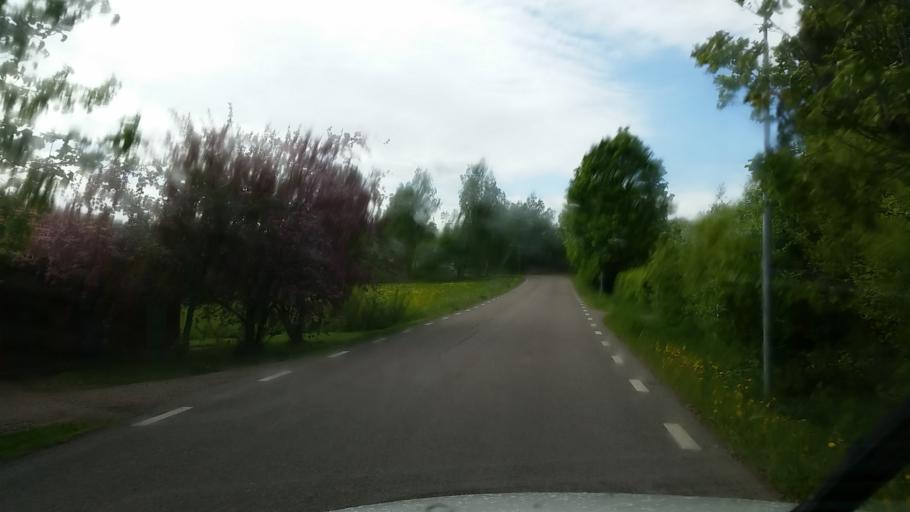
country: SE
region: Dalarna
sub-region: Borlange Kommun
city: Ornas
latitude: 60.5045
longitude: 15.5852
